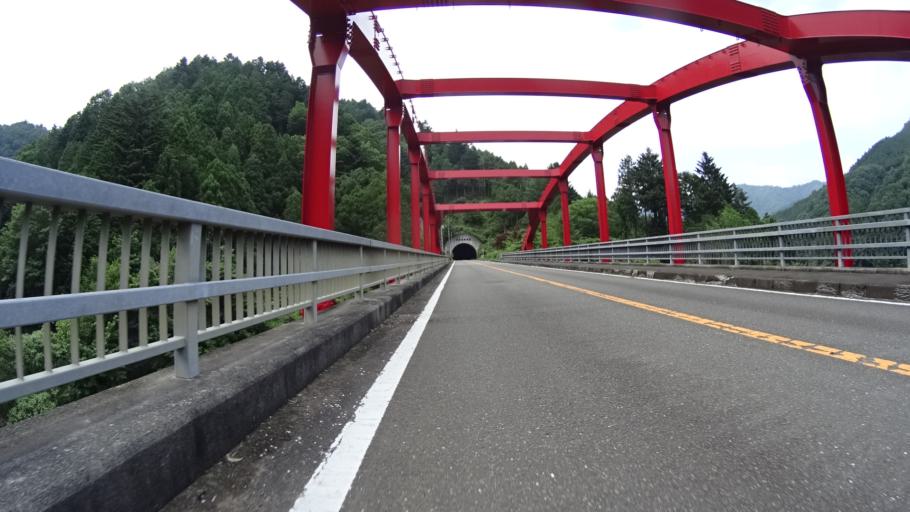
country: JP
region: Kanagawa
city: Hadano
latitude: 35.5092
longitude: 139.2311
